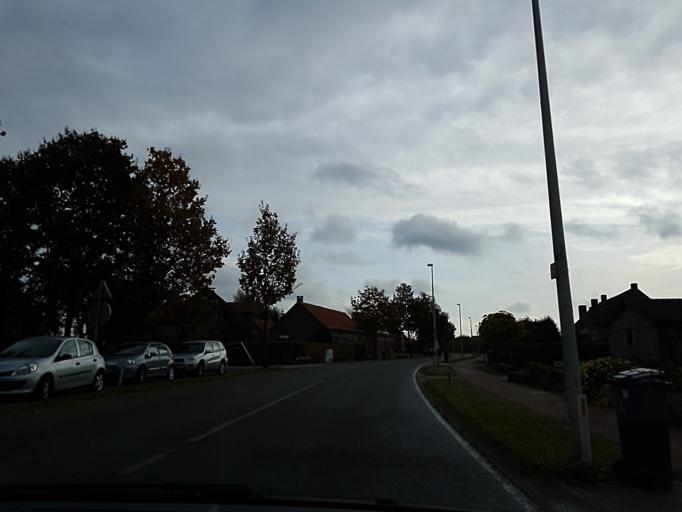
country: BE
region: Flanders
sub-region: Provincie Antwerpen
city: Lier
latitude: 51.1568
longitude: 4.5515
